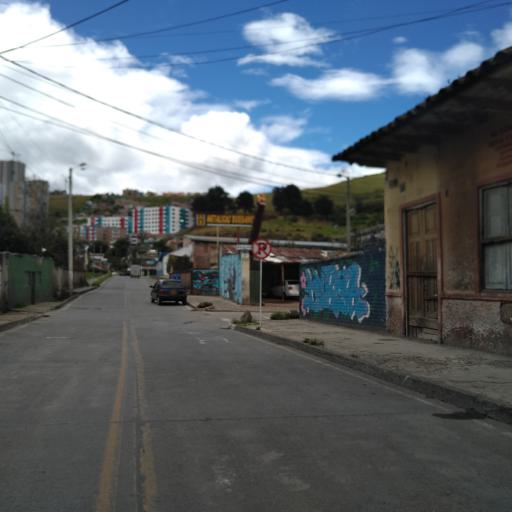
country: CO
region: Narino
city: Pasto
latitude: 1.2123
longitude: -77.2737
